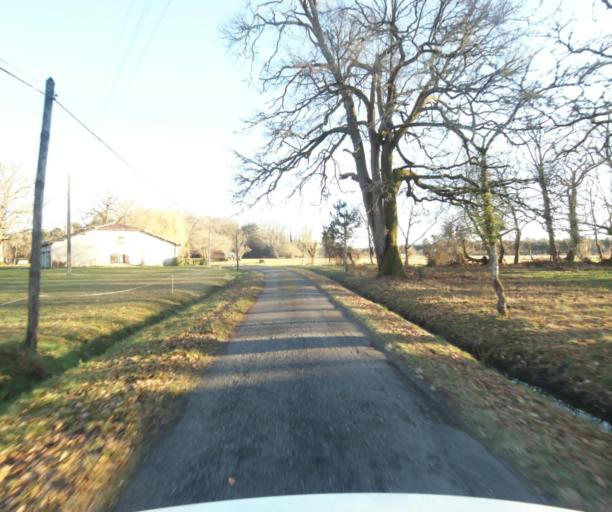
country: FR
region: Aquitaine
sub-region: Departement des Landes
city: Gabarret
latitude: 44.1099
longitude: -0.0821
